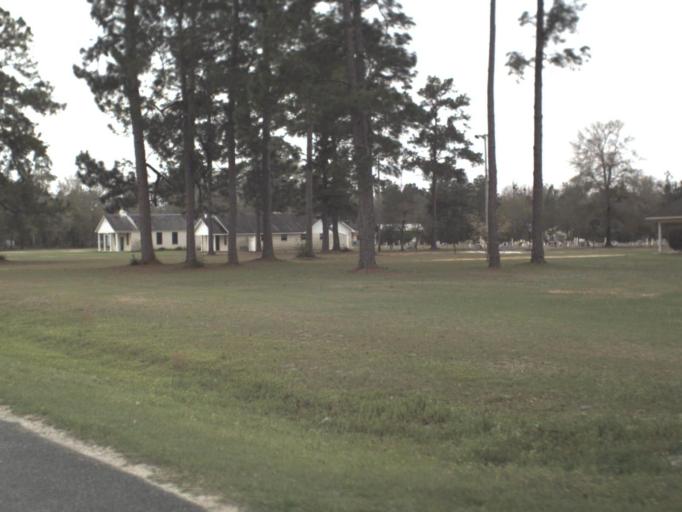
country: US
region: Florida
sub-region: Calhoun County
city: Blountstown
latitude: 30.4522
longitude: -85.1848
